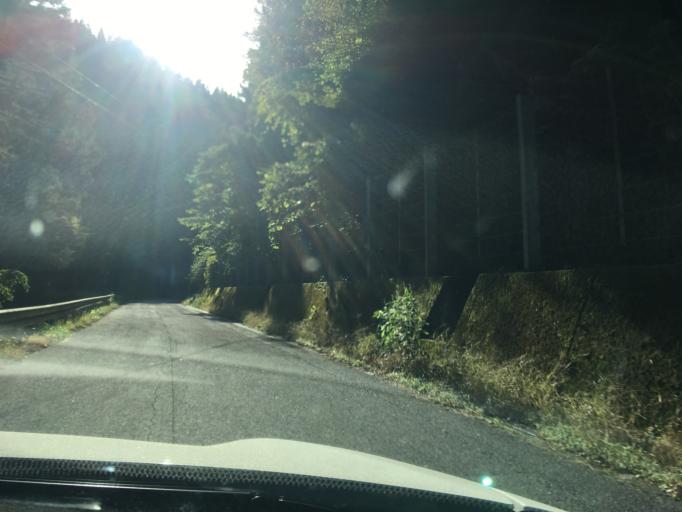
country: JP
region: Fukushima
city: Ishikawa
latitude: 37.1167
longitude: 140.5645
